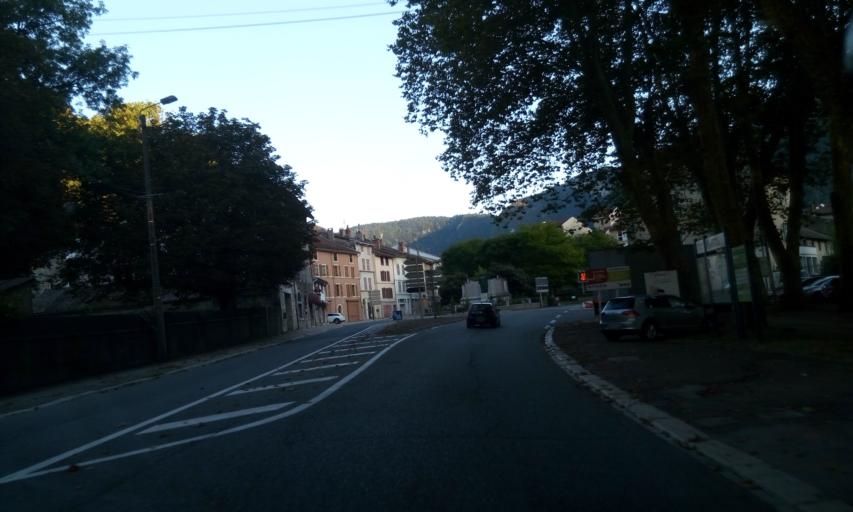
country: FR
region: Rhone-Alpes
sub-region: Departement de l'Ain
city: Nantua
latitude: 46.1572
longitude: 5.6042
